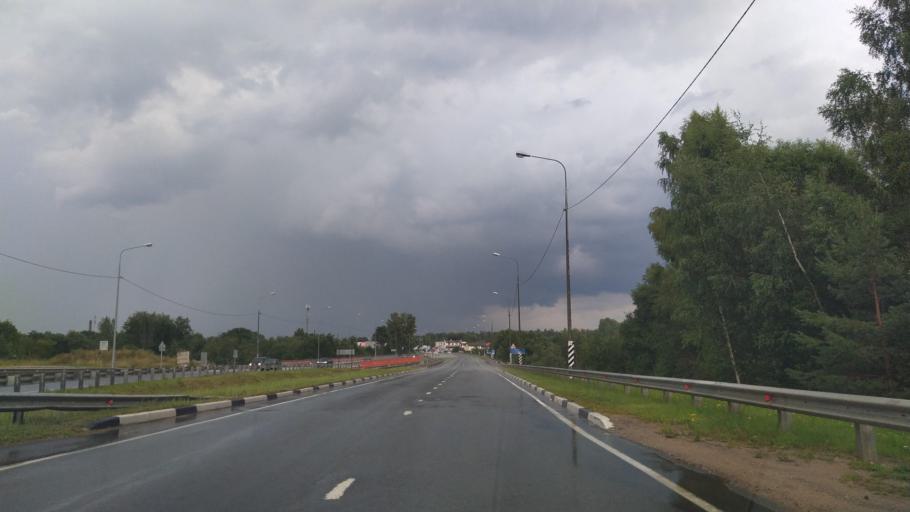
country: RU
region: Pskov
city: Pskov
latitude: 57.7406
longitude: 28.3665
